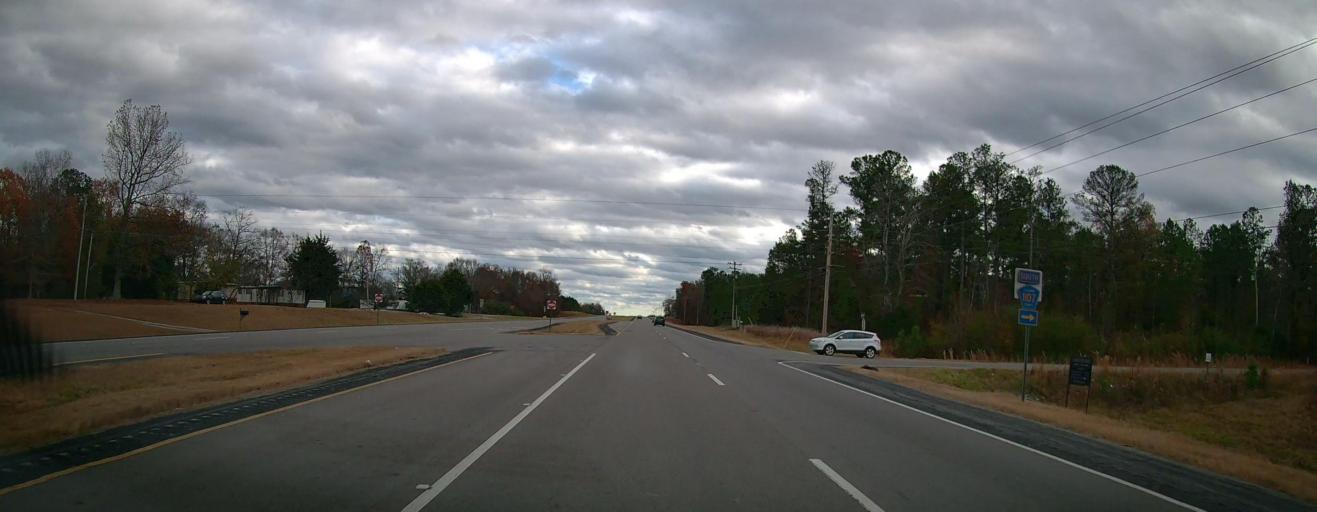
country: US
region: Alabama
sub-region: Morgan County
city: Falkville
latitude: 34.2831
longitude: -86.9974
